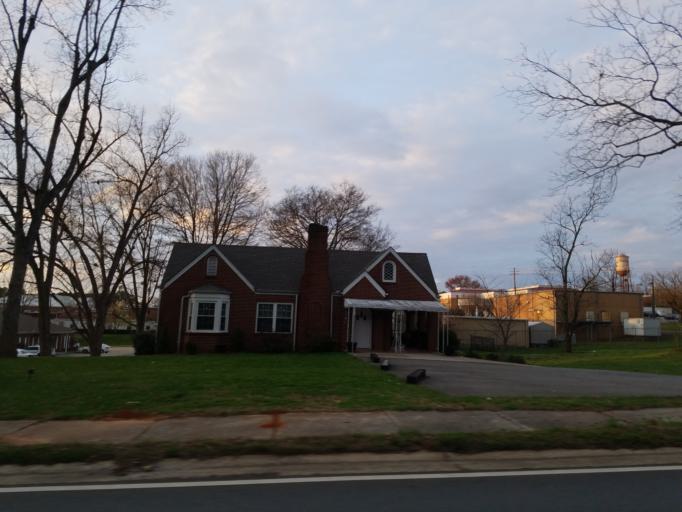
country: US
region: Georgia
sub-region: Pickens County
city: Jasper
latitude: 34.4674
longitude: -84.4314
